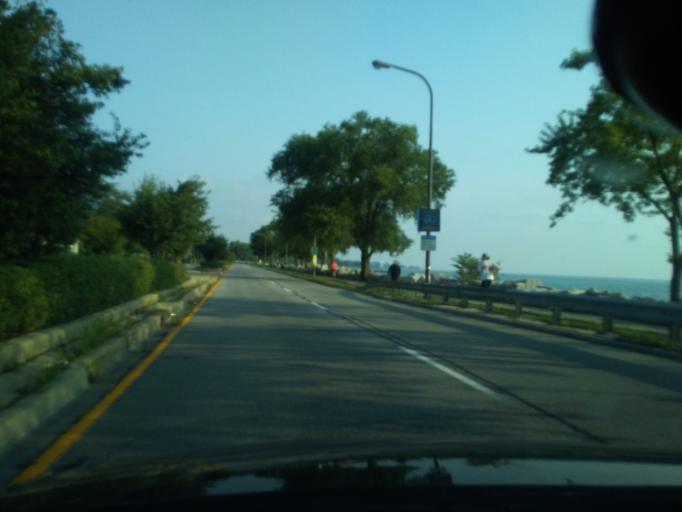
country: US
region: Illinois
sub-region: Cook County
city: Evanston
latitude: 42.0233
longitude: -87.6654
